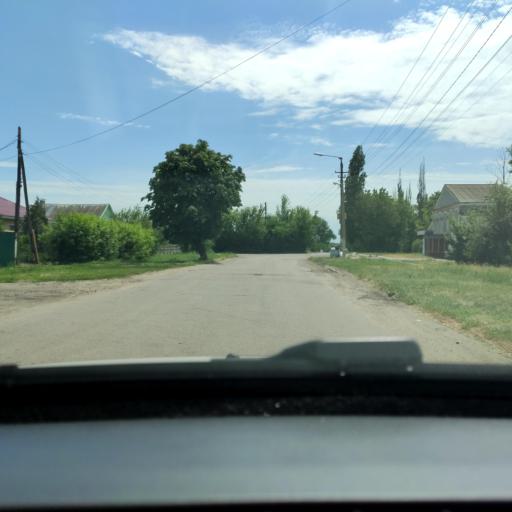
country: RU
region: Voronezj
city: Maslovka
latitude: 51.5063
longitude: 39.2939
